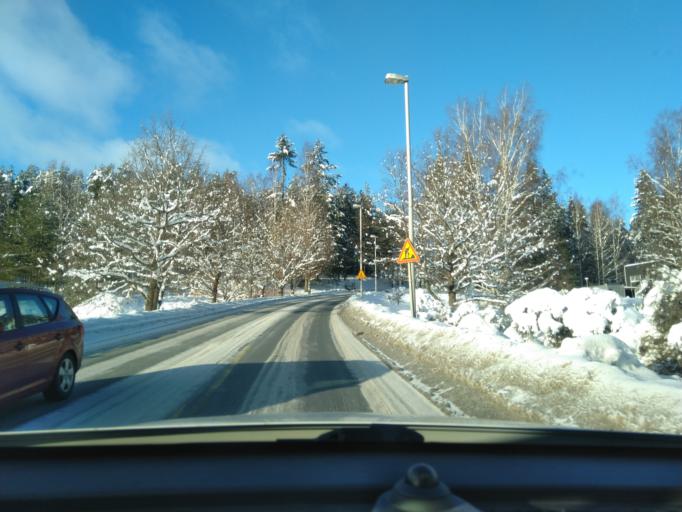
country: FI
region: Haeme
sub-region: Haemeenlinna
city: Haemeenlinna
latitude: 60.9869
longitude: 24.4179
